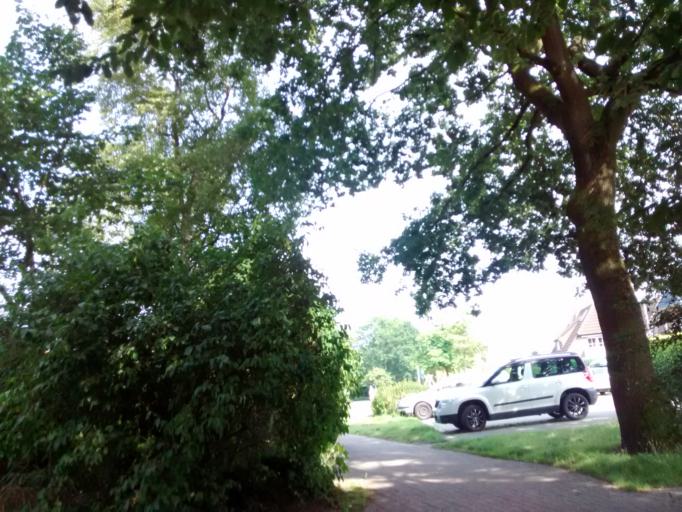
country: DE
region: Lower Saxony
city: Varel
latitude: 53.4471
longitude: 8.1152
